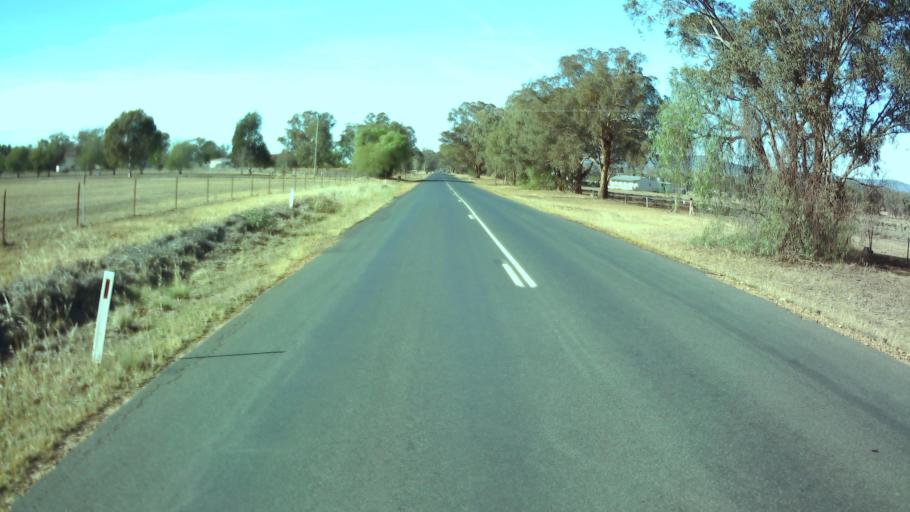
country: AU
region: New South Wales
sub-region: Weddin
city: Grenfell
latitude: -33.9080
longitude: 148.1460
